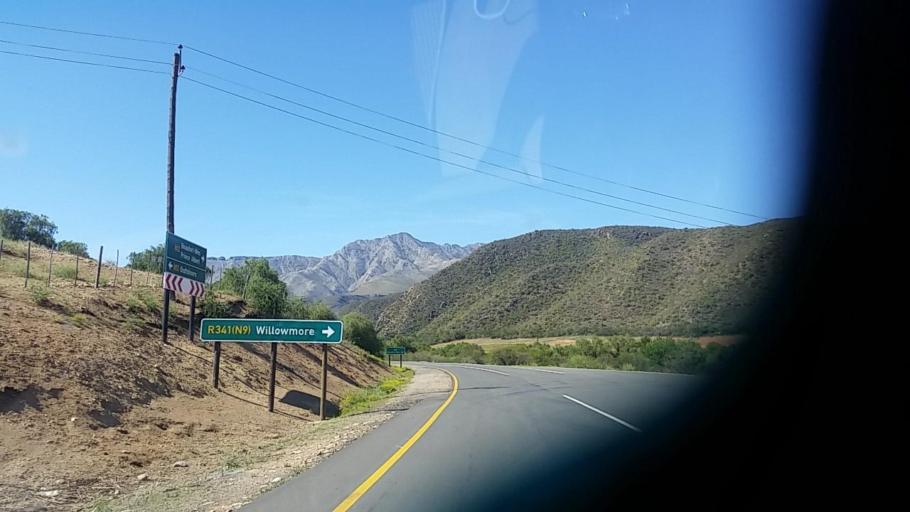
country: ZA
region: Western Cape
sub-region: Eden District Municipality
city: Oudtshoorn
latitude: -33.4865
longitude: 22.5421
